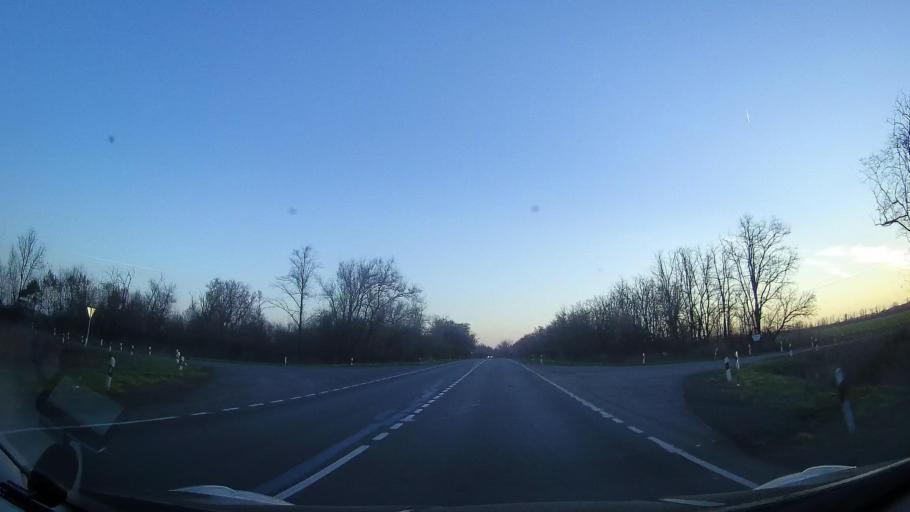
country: RU
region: Rostov
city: Bagayevskaya
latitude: 47.1050
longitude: 40.2767
